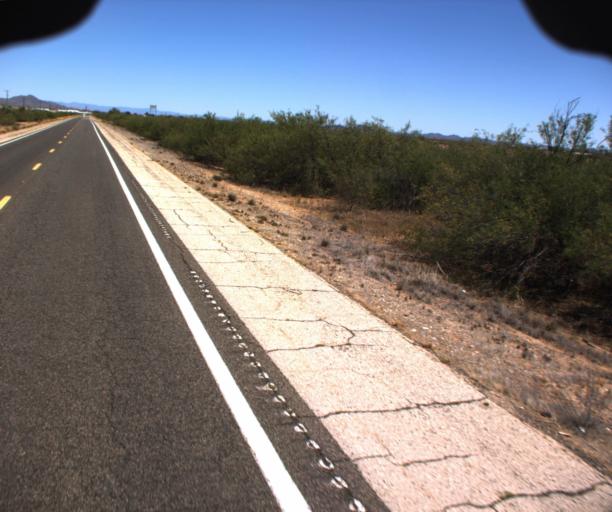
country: US
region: Arizona
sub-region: Yavapai County
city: Congress
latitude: 33.9346
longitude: -113.2065
